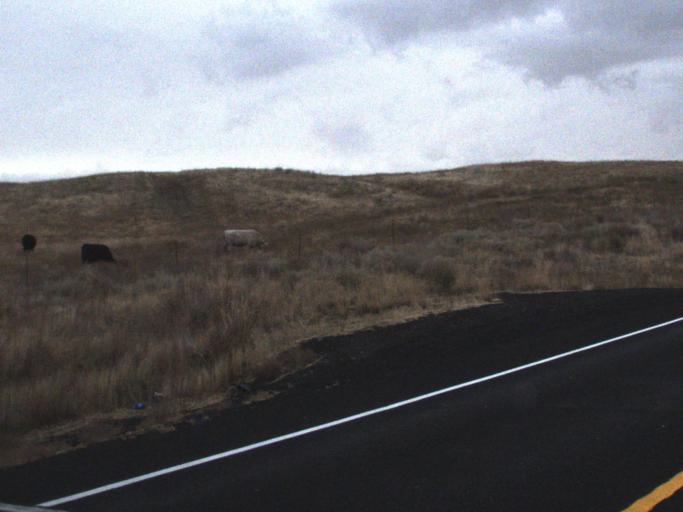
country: US
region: Washington
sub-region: Garfield County
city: Pomeroy
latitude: 46.7884
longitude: -117.9026
